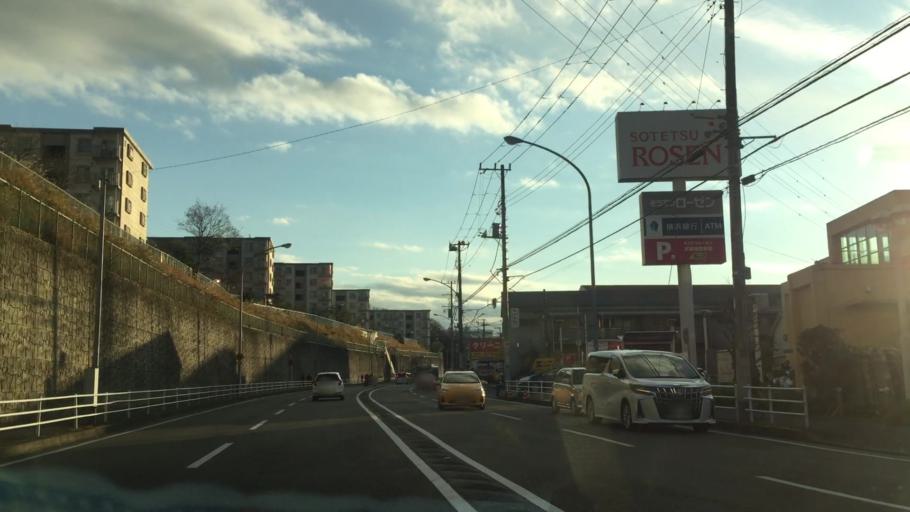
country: JP
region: Kanagawa
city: Zushi
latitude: 35.3405
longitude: 139.6112
